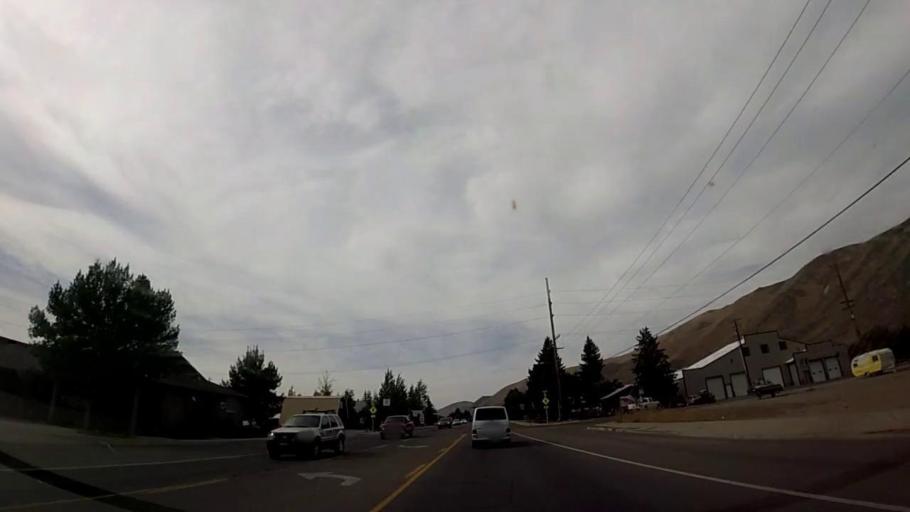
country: US
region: Idaho
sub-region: Blaine County
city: Bellevue
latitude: 43.4702
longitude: -114.2635
